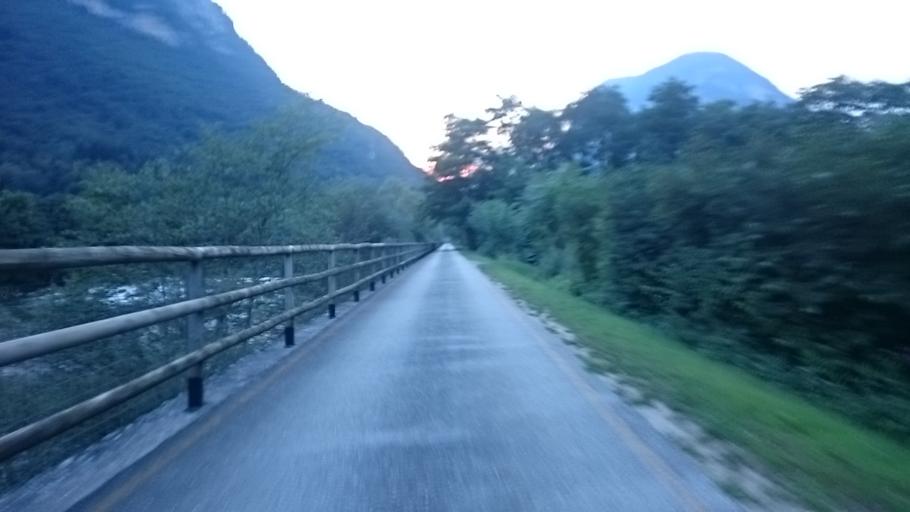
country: IT
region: Trentino-Alto Adige
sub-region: Provincia di Trento
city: Grigno
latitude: 46.0004
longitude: 11.6534
